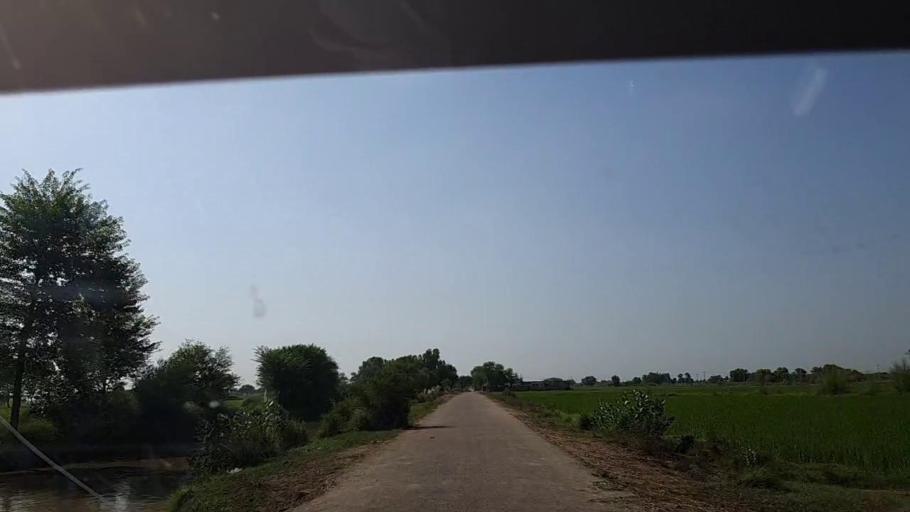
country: PK
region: Sindh
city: Tangwani
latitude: 28.2084
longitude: 69.0276
